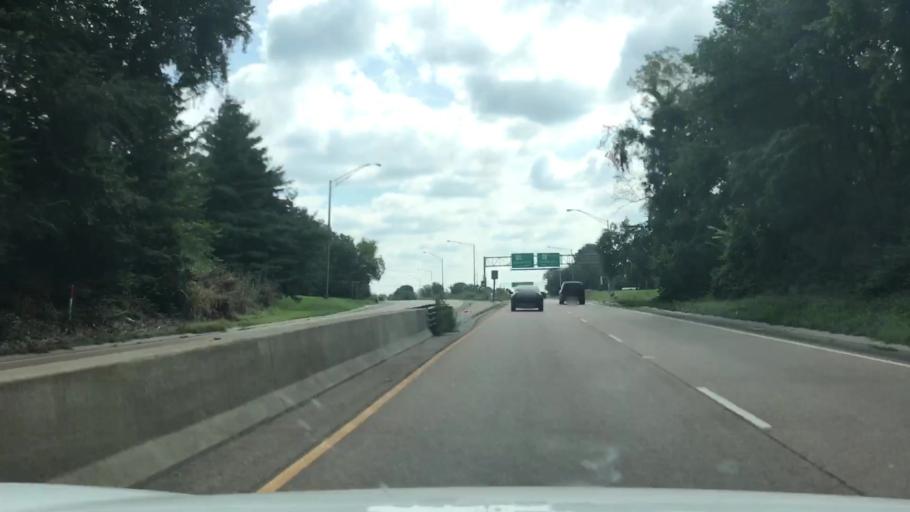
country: US
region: Illinois
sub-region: Saint Clair County
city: Alorton
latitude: 38.5516
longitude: -90.0723
